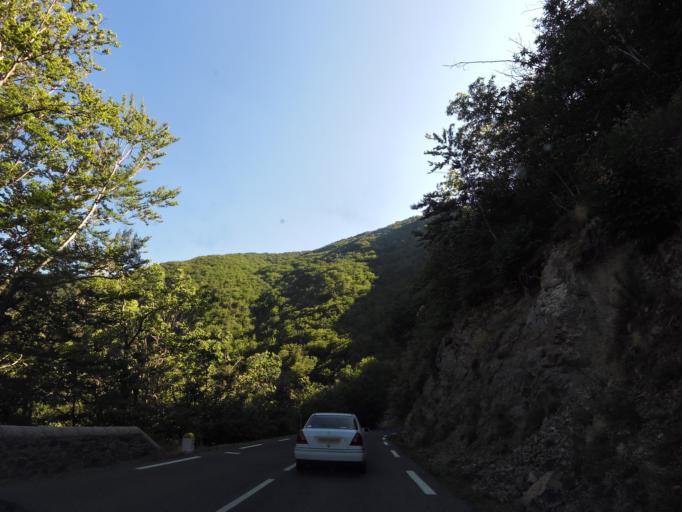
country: FR
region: Languedoc-Roussillon
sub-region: Departement du Gard
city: Valleraugue
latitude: 44.0877
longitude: 3.5760
